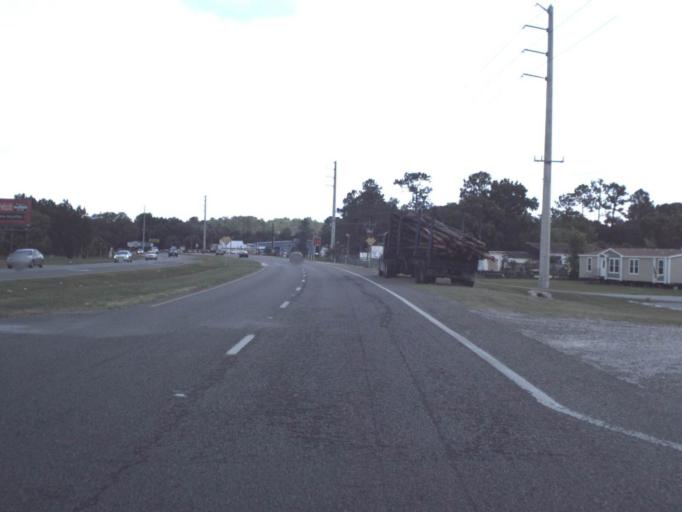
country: US
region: Florida
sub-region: Putnam County
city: East Palatka
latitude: 29.6397
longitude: -81.5899
